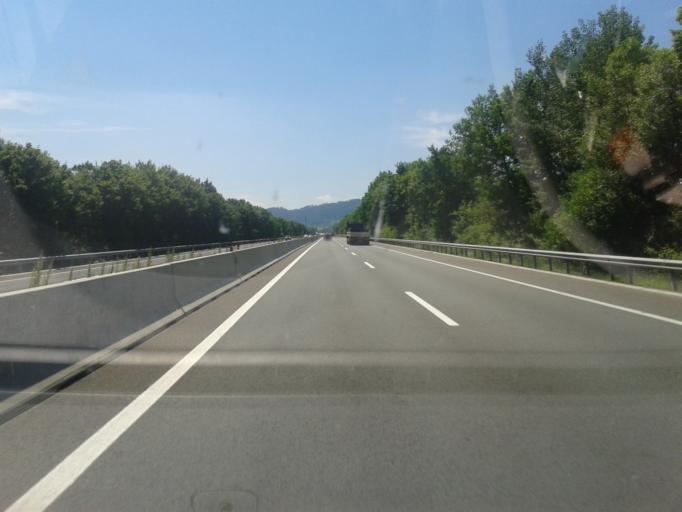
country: AT
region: Carinthia
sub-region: Politischer Bezirk Wolfsberg
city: Sankt Andrae
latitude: 46.7996
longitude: 14.8196
